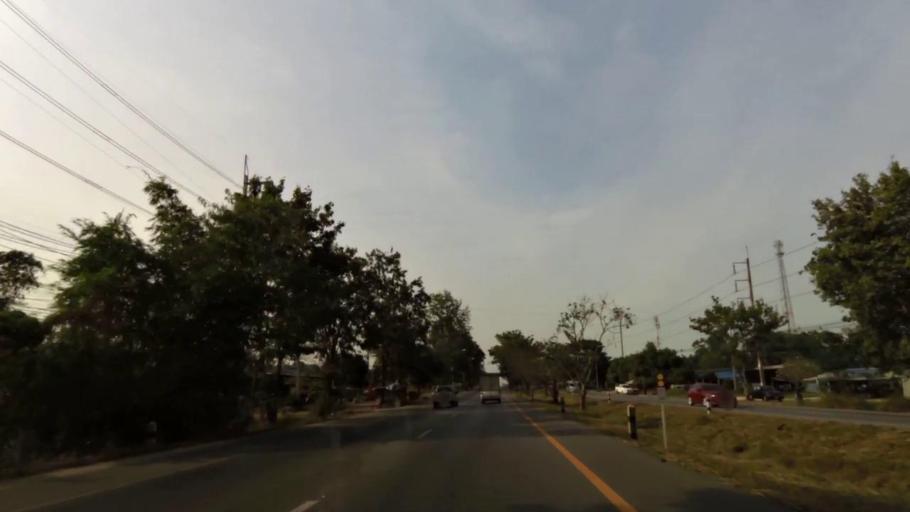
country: TH
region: Chon Buri
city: Ban Bueng
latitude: 13.2425
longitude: 101.2125
